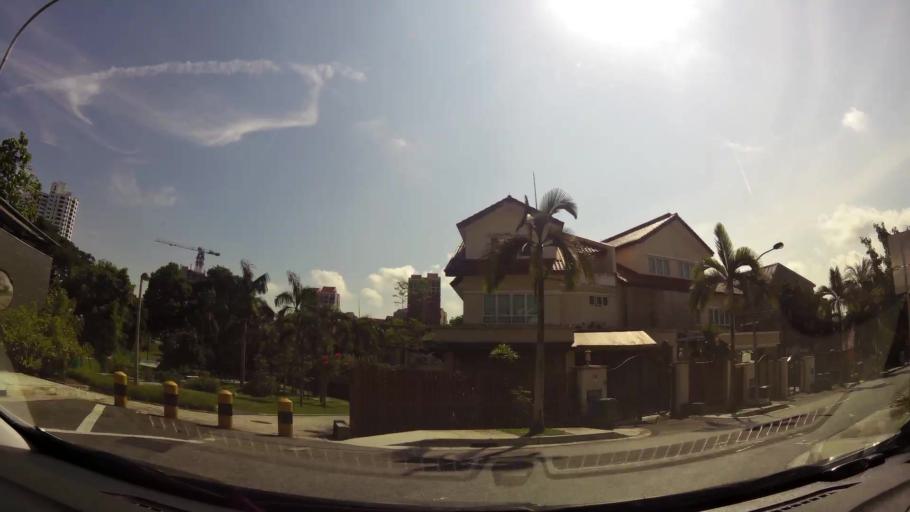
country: SG
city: Singapore
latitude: 1.3585
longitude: 103.8271
